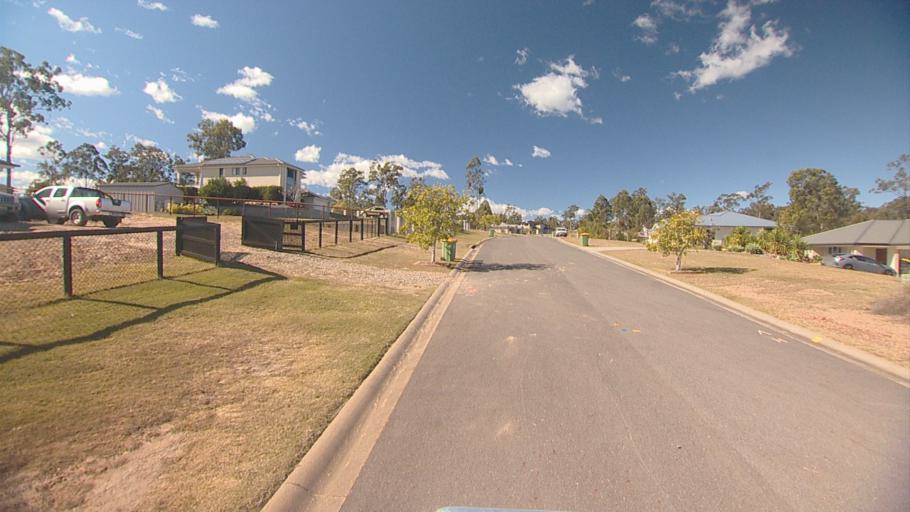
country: AU
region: Queensland
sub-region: Logan
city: North Maclean
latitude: -27.7547
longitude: 152.9333
